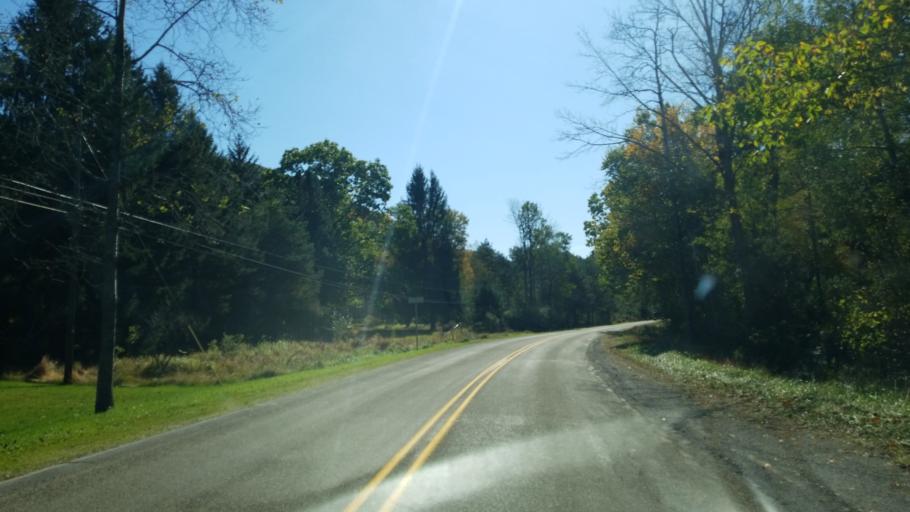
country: US
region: Pennsylvania
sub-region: Elk County
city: Saint Marys
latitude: 41.2836
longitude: -78.3941
